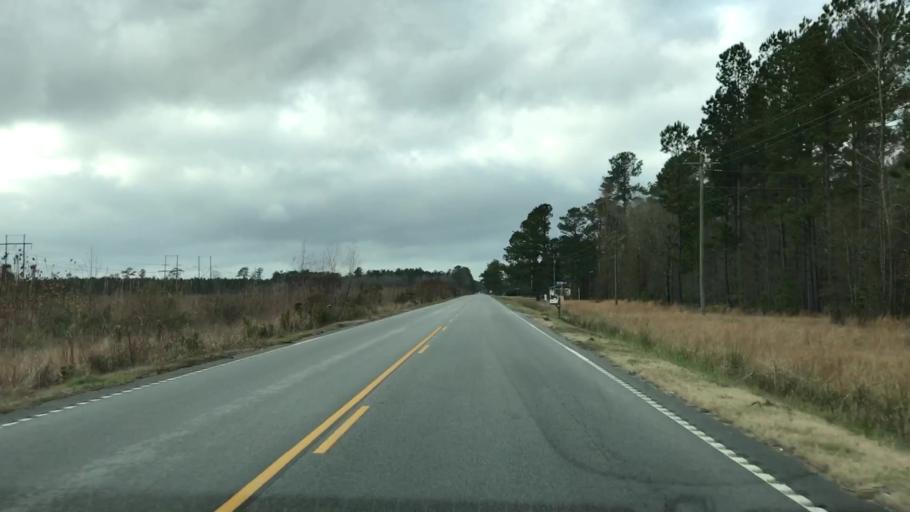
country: US
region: South Carolina
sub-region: Berkeley County
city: Saint Stephen
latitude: 33.2822
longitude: -79.7348
